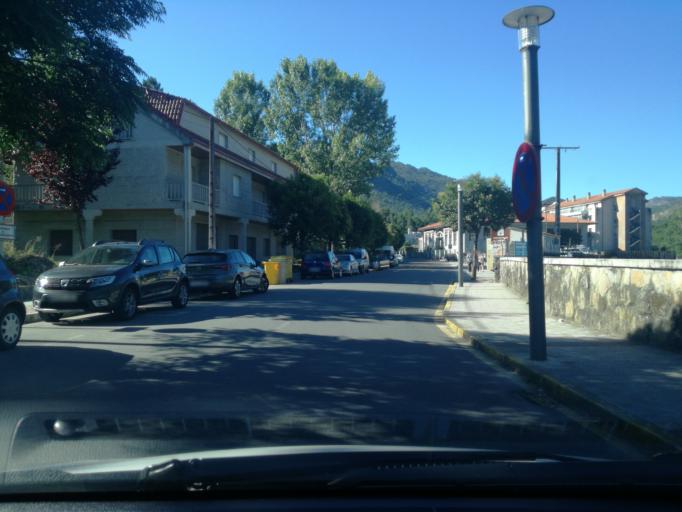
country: ES
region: Galicia
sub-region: Provincia de Ourense
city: Lobios
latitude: 41.8629
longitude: -8.1063
